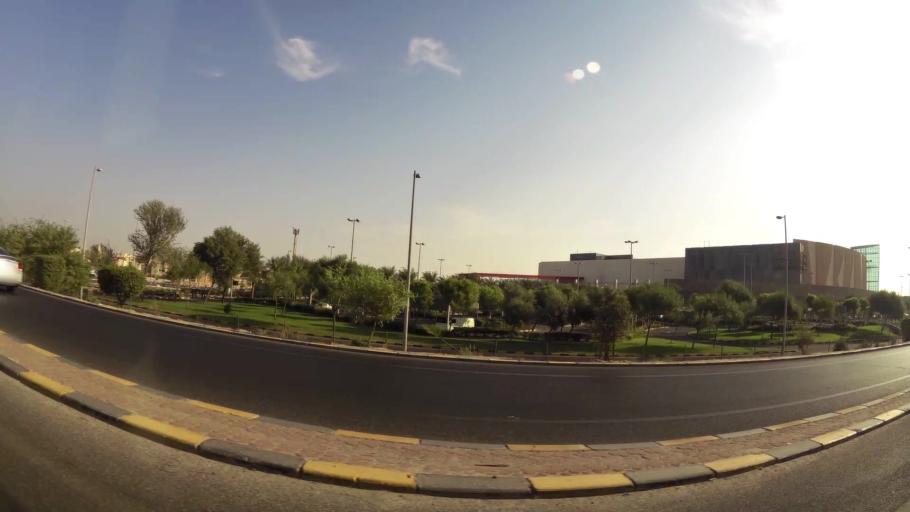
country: KW
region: Al Farwaniyah
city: Janub as Surrah
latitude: 29.2672
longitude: 47.9899
